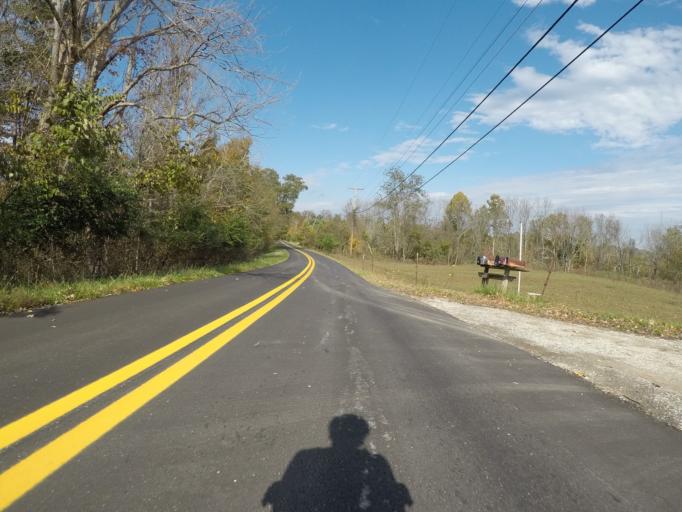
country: US
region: West Virginia
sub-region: Cabell County
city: Huntington
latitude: 38.3781
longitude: -82.4252
